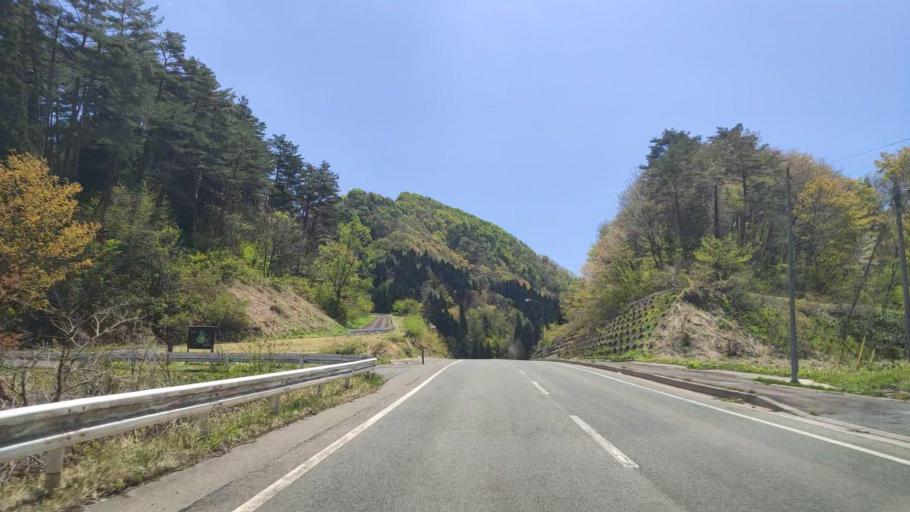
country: JP
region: Yamagata
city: Shinjo
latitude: 38.9008
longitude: 140.3278
